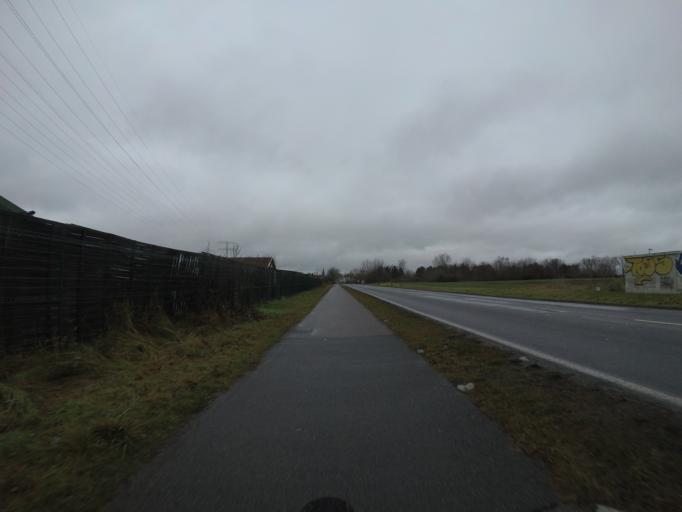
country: DE
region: Brandenburg
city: Ahrensfelde
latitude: 52.5561
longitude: 13.5910
